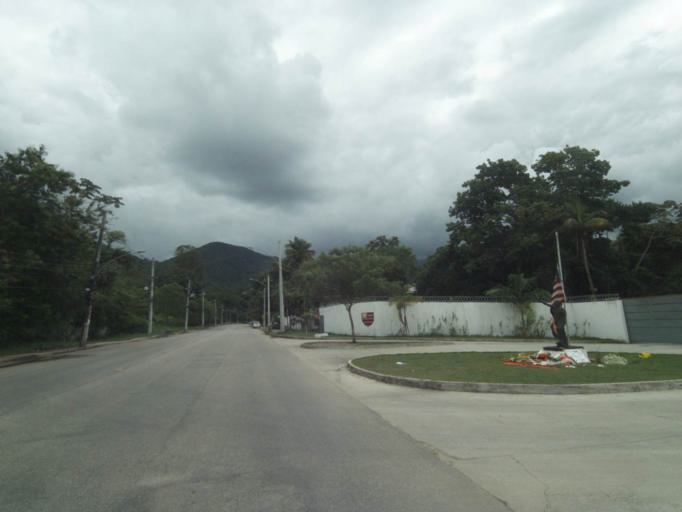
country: BR
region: Rio de Janeiro
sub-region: Nilopolis
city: Nilopolis
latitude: -22.9843
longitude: -43.5060
